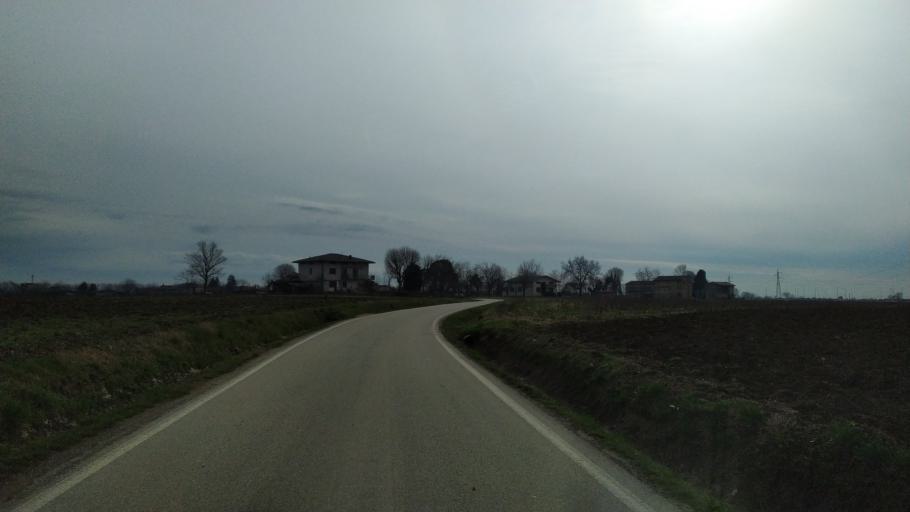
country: IT
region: Veneto
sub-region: Provincia di Vicenza
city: Malo
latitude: 45.6545
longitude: 11.4409
